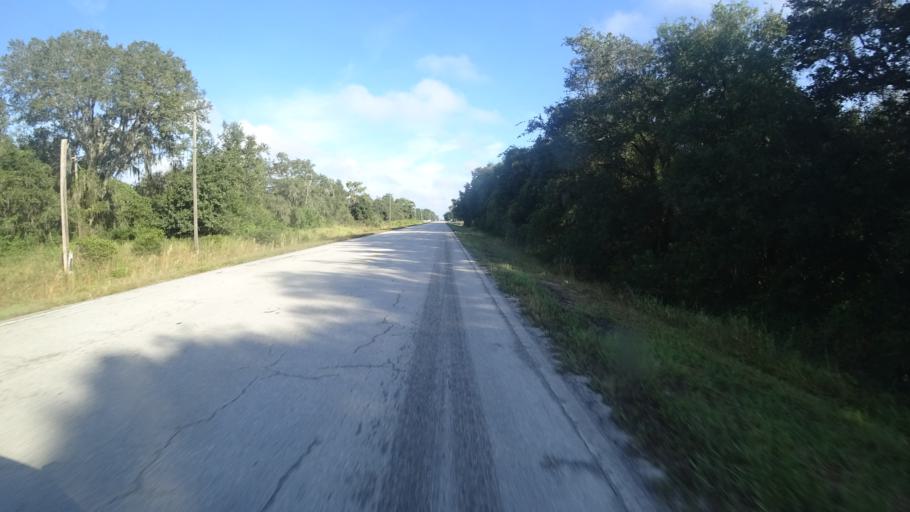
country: US
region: Florida
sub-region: Sarasota County
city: The Meadows
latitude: 27.4527
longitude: -82.3033
